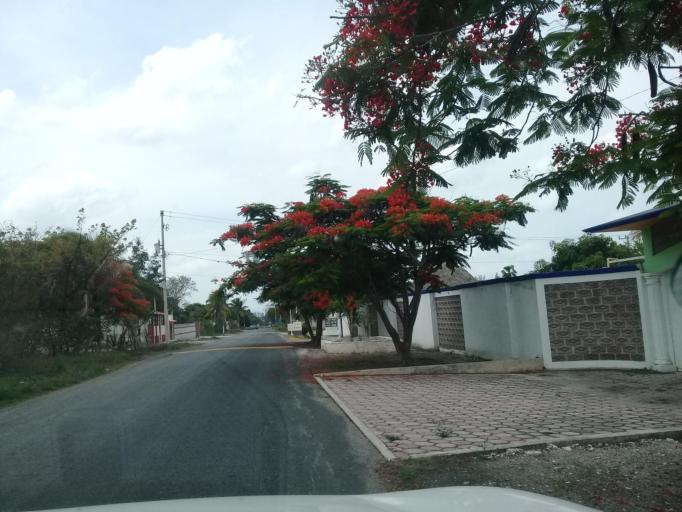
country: MX
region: Veracruz
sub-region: Emiliano Zapata
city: Plan del Rio
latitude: 19.3556
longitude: -96.6586
